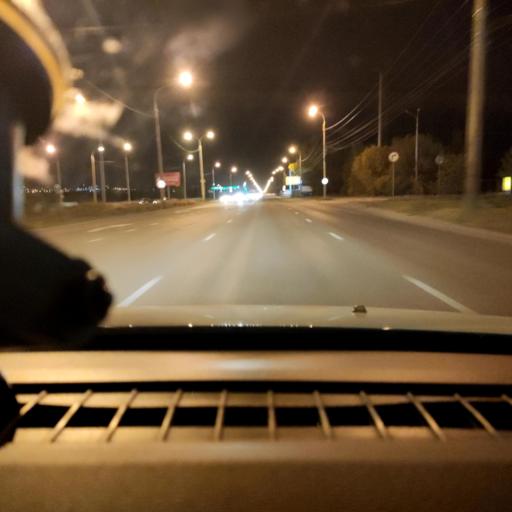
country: RU
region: Samara
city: Samara
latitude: 53.1423
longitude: 50.1802
